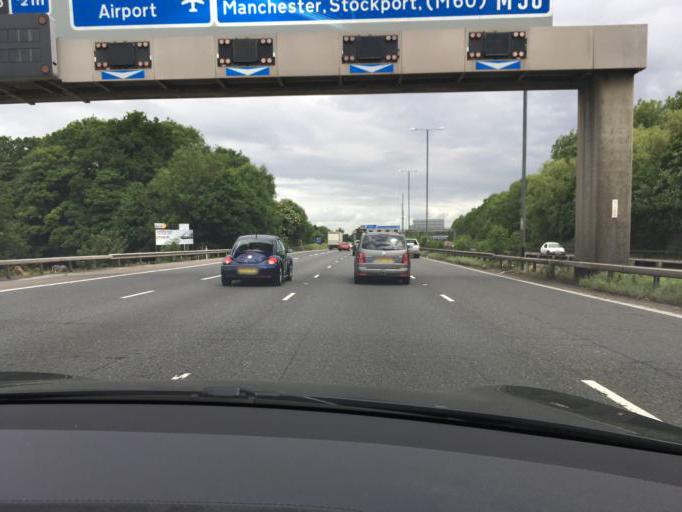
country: GB
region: England
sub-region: Manchester
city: Ringway
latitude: 53.3666
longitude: -2.2945
